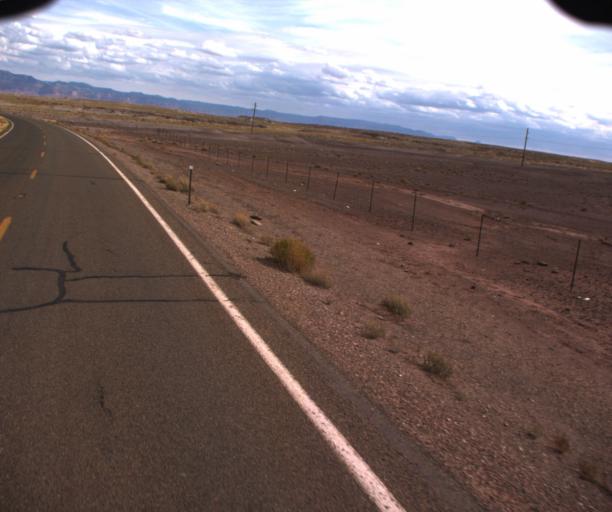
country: US
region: Arizona
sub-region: Apache County
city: Many Farms
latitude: 36.4697
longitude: -109.5268
